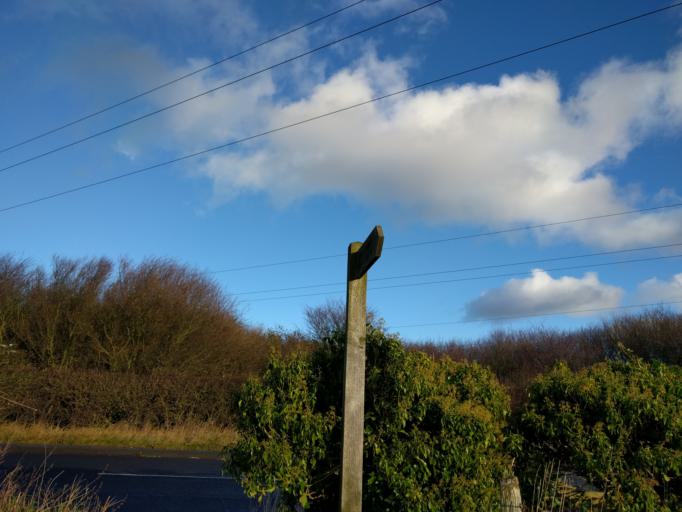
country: GB
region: England
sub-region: Northumberland
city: Bedlington
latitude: 55.1204
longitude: -1.5762
